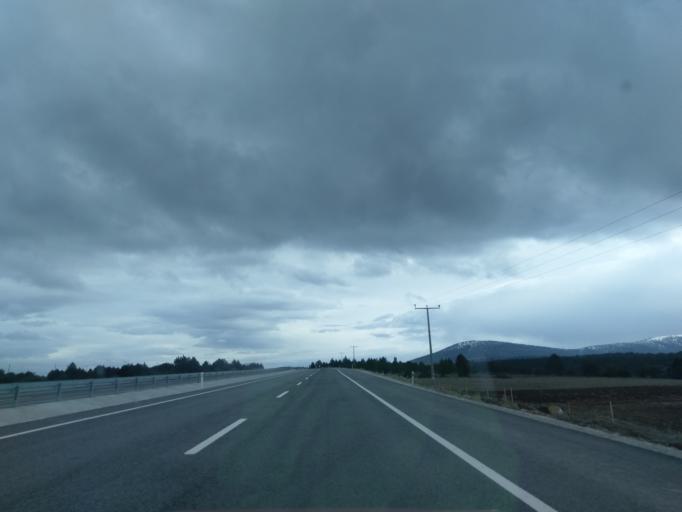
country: TR
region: Kuetahya
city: Cavdarhisar
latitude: 39.2236
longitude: 29.7290
